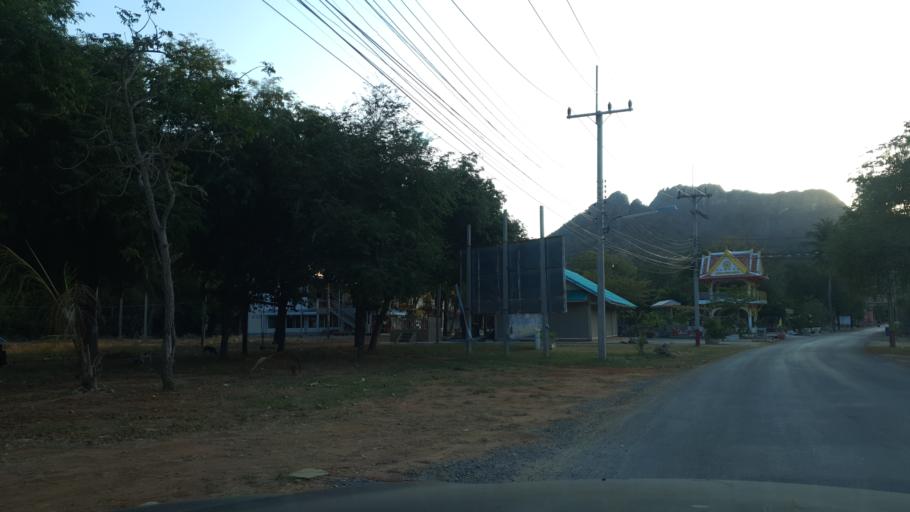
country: TH
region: Prachuap Khiri Khan
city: Sam Roi Yot
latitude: 12.2043
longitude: 100.0082
